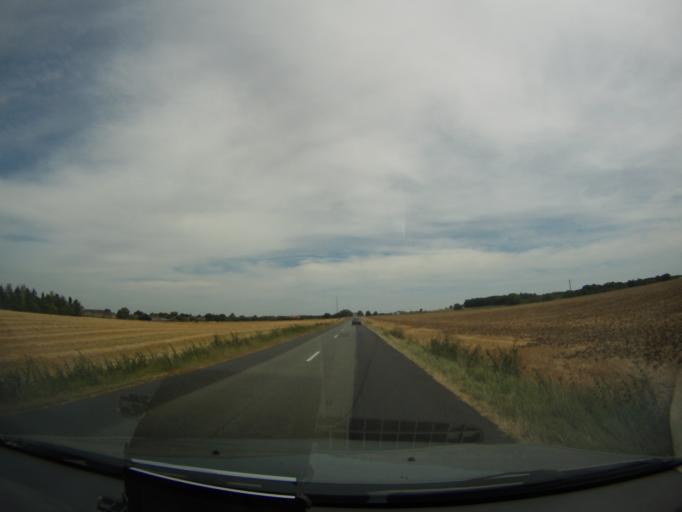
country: FR
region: Poitou-Charentes
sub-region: Departement de la Vienne
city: Mirebeau
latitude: 46.7669
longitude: 0.1505
